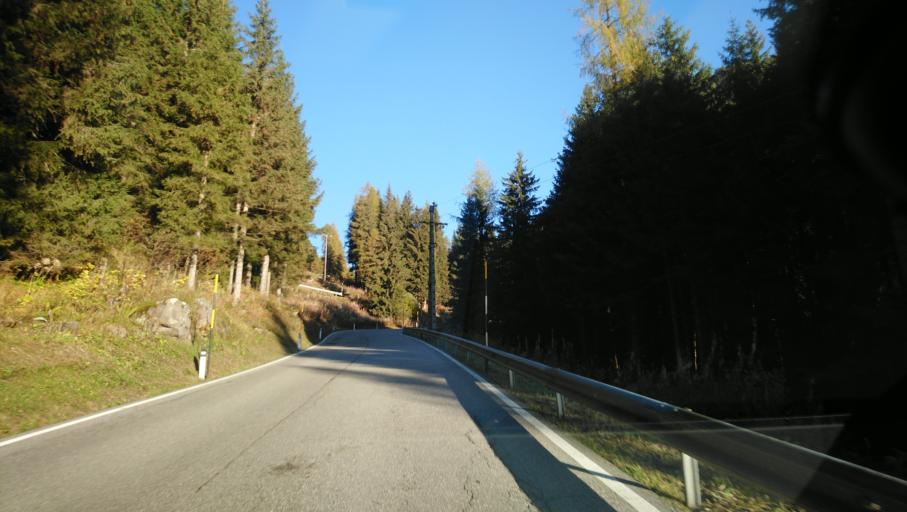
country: IT
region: Veneto
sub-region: Provincia di Belluno
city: Falcade Alto
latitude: 46.3668
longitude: 11.8304
